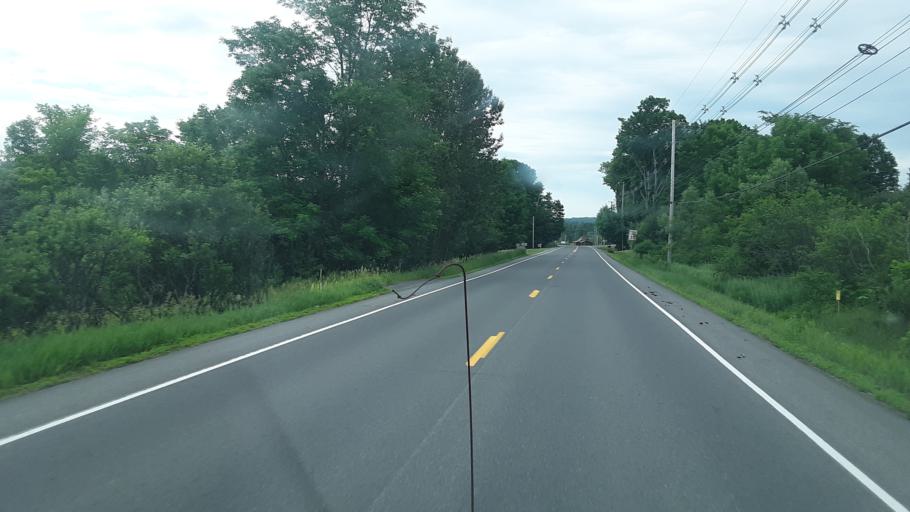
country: US
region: Maine
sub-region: Penobscot County
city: Patten
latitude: 45.8794
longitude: -68.4181
